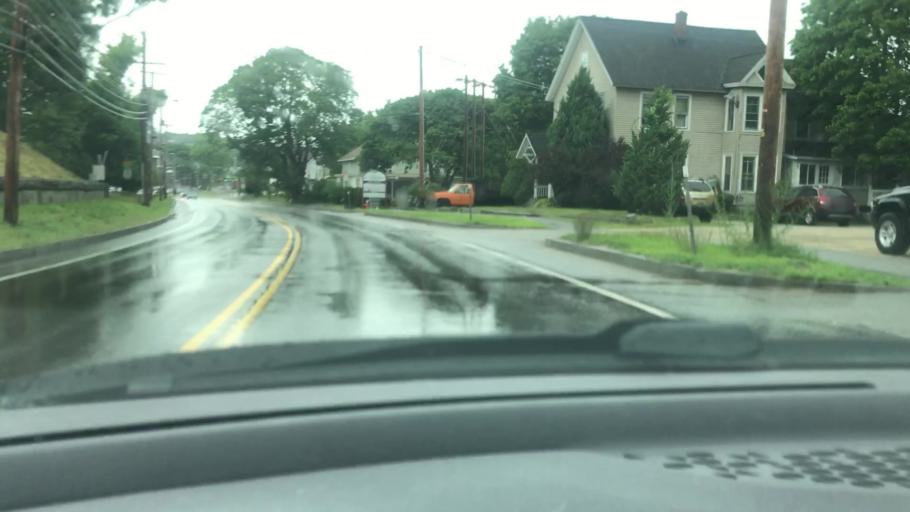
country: US
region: New Hampshire
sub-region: Merrimack County
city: Concord
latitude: 43.2245
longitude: -71.5531
